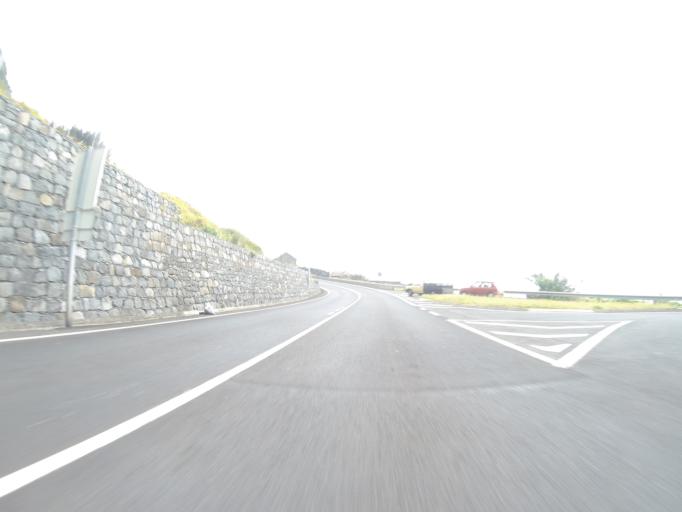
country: PT
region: Madeira
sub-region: Porto Moniz
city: Porto Moniz
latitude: 32.8436
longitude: -17.1440
